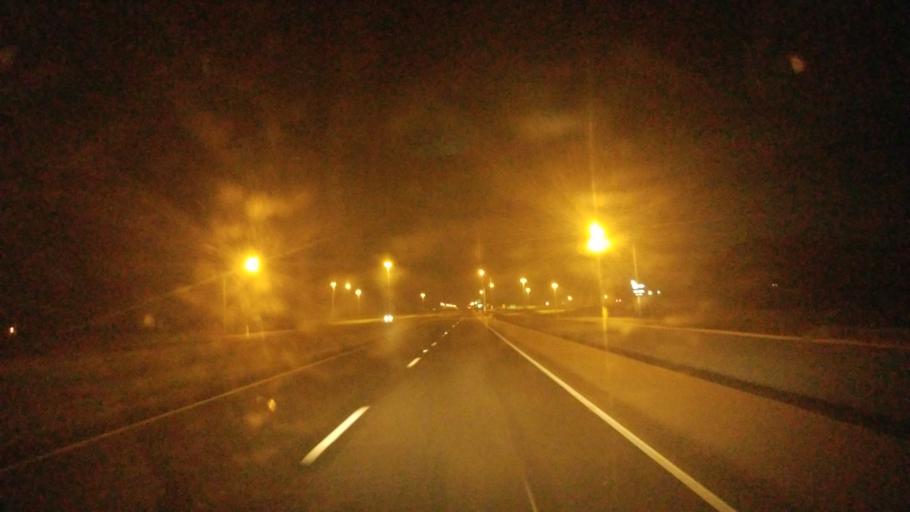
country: US
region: Indiana
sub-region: Vigo County
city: Seelyville
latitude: 39.4308
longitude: -87.3242
